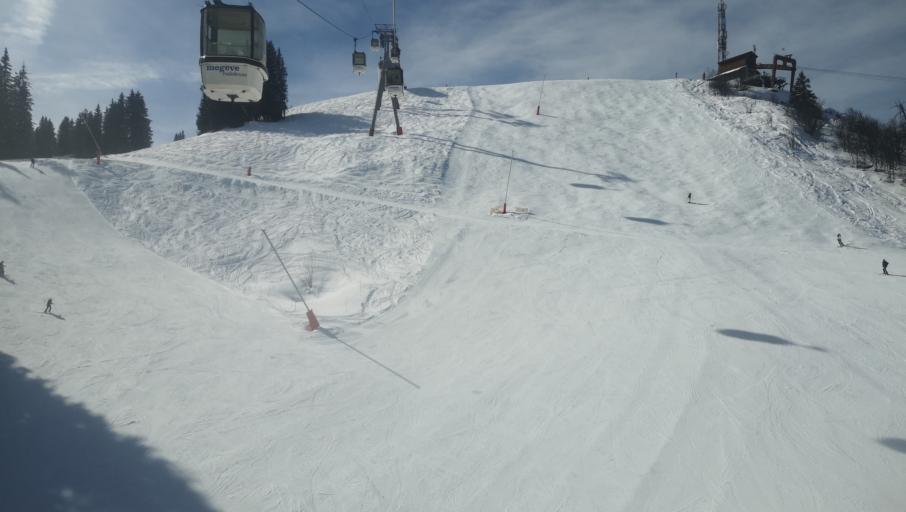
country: FR
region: Rhone-Alpes
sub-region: Departement de la Haute-Savoie
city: Megeve
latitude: 45.8345
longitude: 6.6161
